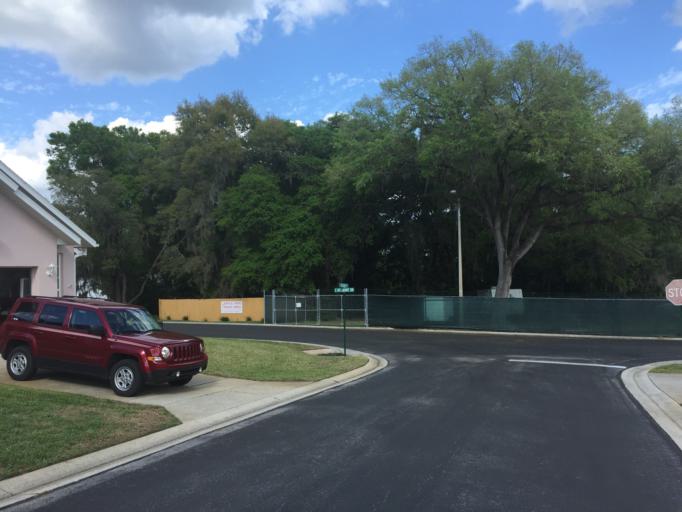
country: US
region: Florida
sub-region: Citrus County
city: Inverness Highlands South
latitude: 28.8115
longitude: -82.3210
